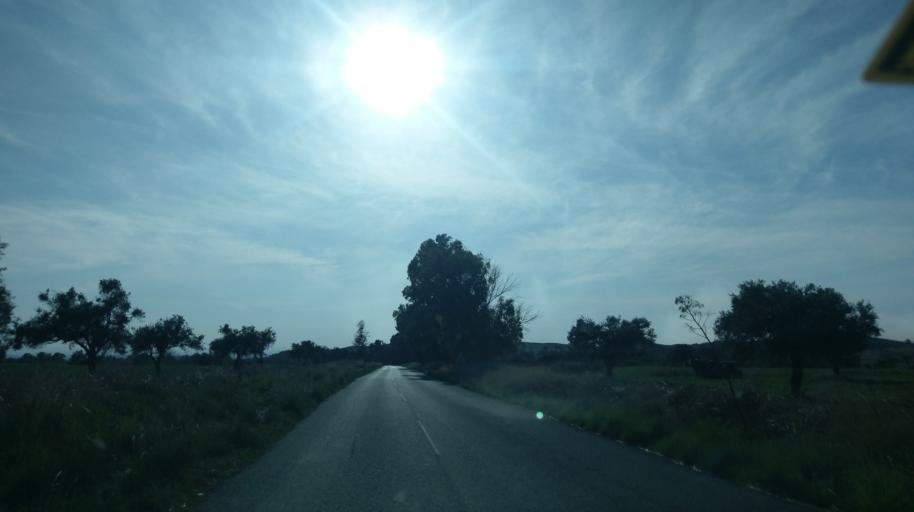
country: CY
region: Ammochostos
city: Lefkonoiko
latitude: 35.2975
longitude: 33.7413
